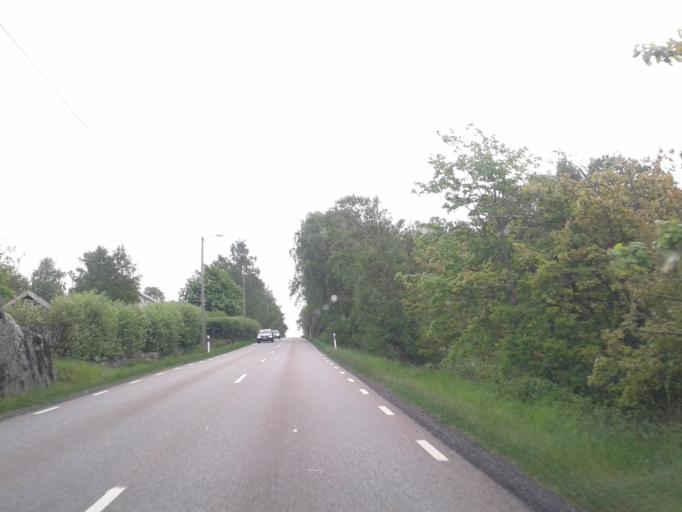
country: SE
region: Vaestra Goetaland
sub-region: Kungalvs Kommun
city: Kode
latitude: 57.8969
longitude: 11.7338
